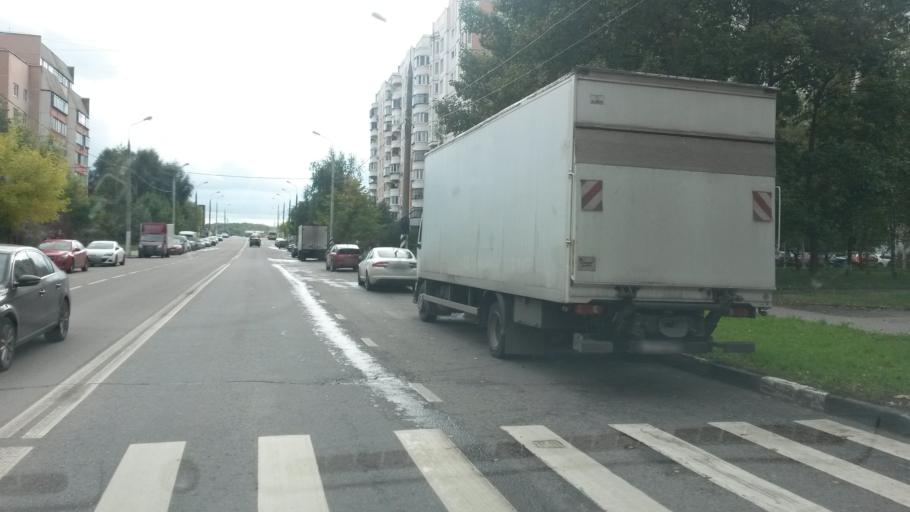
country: RU
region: Moskovskaya
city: Kommunarka
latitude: 55.5317
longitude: 37.5184
